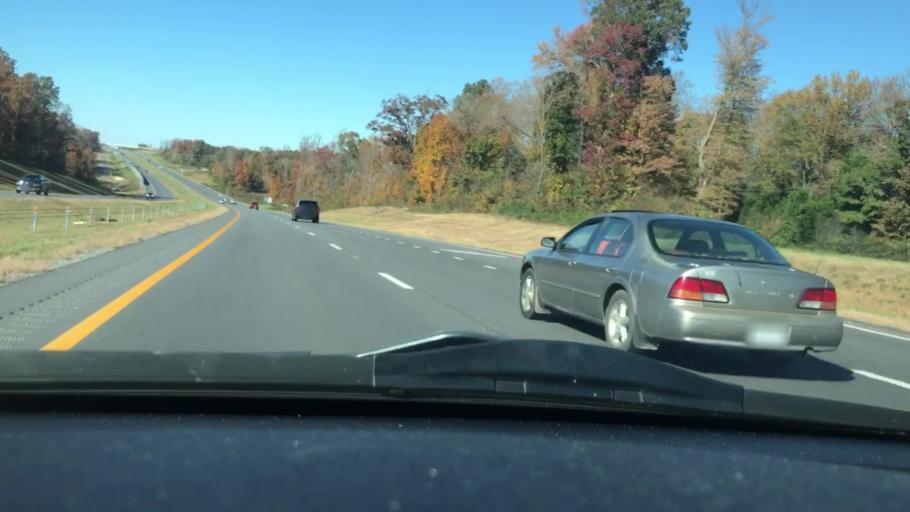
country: US
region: North Carolina
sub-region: Guilford County
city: Summerfield
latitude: 36.2522
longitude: -79.9224
